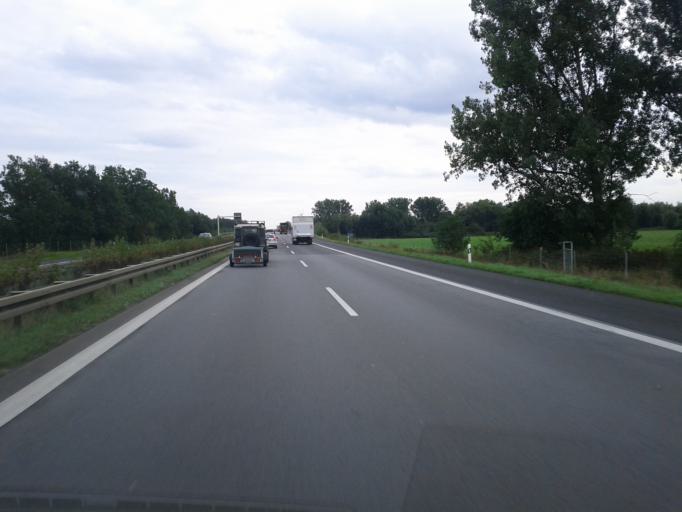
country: DE
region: Brandenburg
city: Mittenwalde
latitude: 52.2846
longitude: 13.5644
